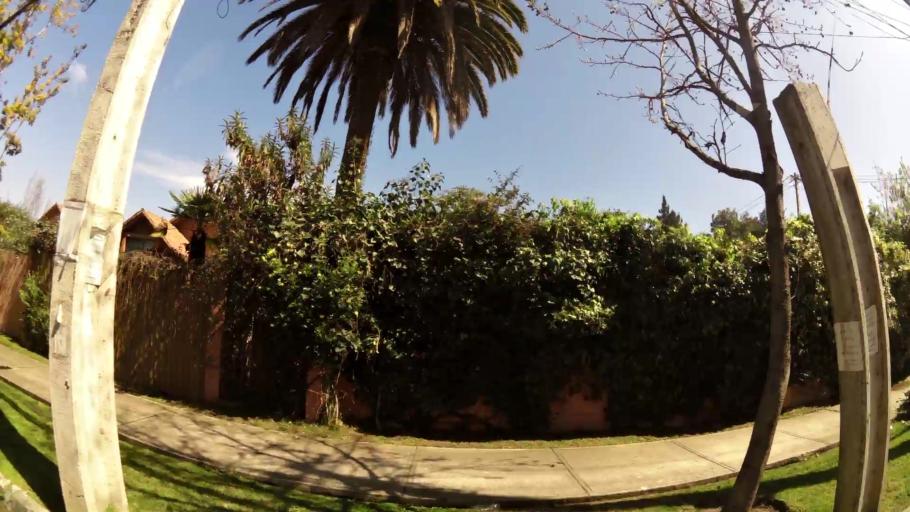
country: CL
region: Santiago Metropolitan
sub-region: Provincia de Santiago
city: Villa Presidente Frei, Nunoa, Santiago, Chile
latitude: -33.4396
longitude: -70.5236
